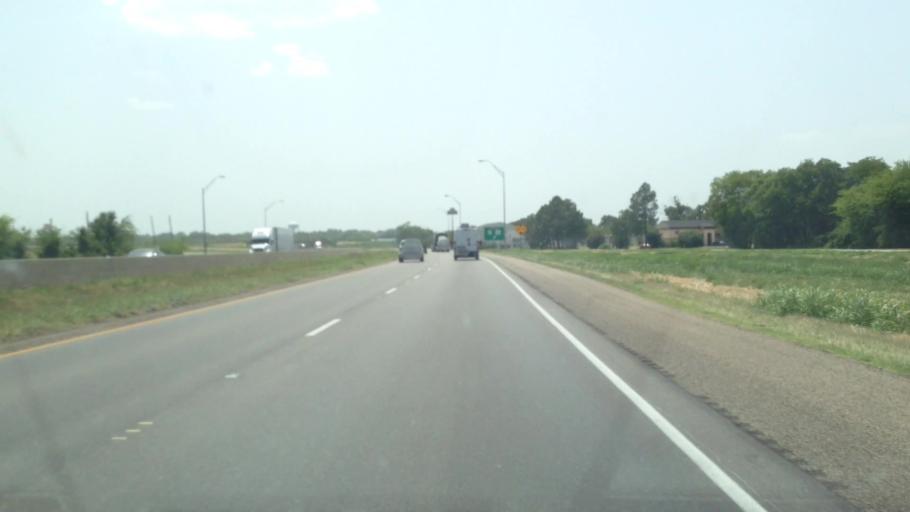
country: US
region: Texas
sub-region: Hopkins County
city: Sulphur Springs
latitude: 33.1453
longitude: -95.5580
